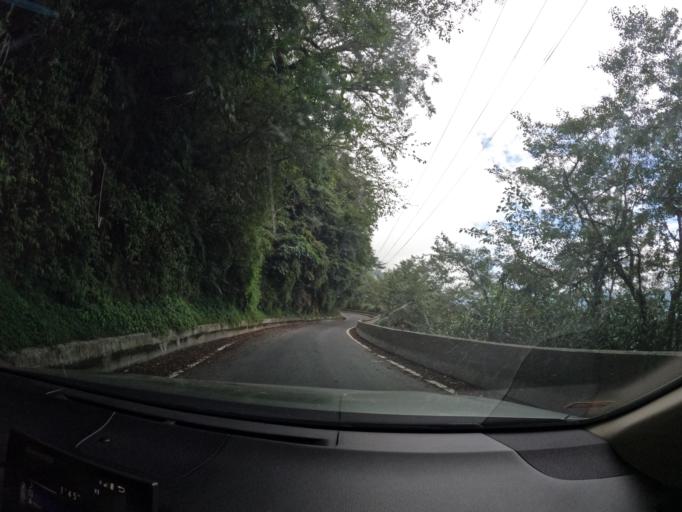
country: TW
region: Taiwan
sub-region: Taitung
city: Taitung
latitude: 23.2411
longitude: 121.0003
